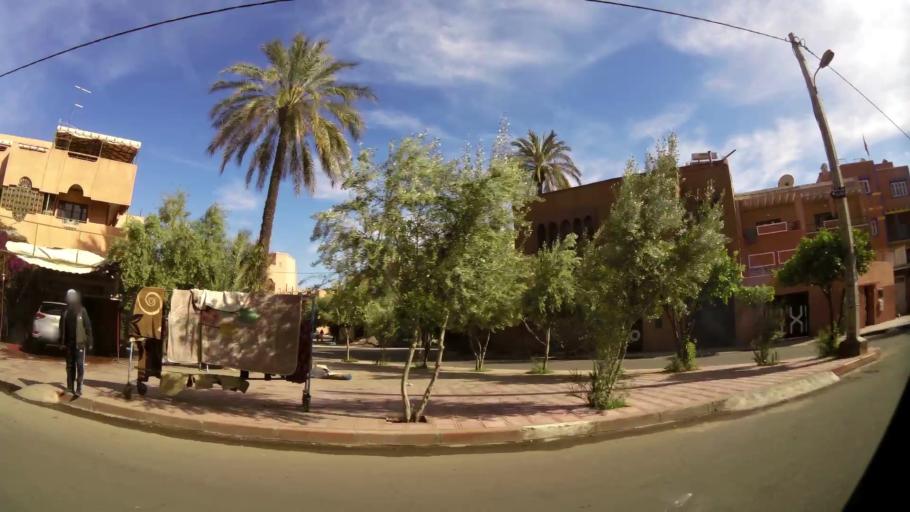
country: MA
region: Marrakech-Tensift-Al Haouz
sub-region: Marrakech
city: Marrakesh
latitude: 31.6540
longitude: -8.0069
